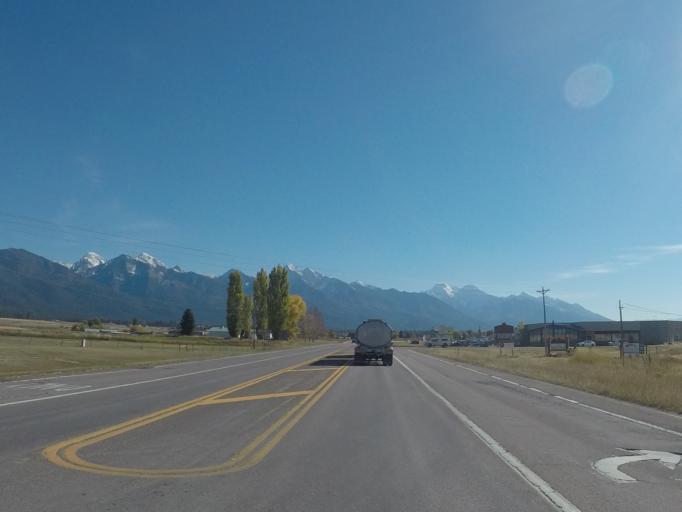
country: US
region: Montana
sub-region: Lake County
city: Ronan
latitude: 47.5381
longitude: -114.1029
